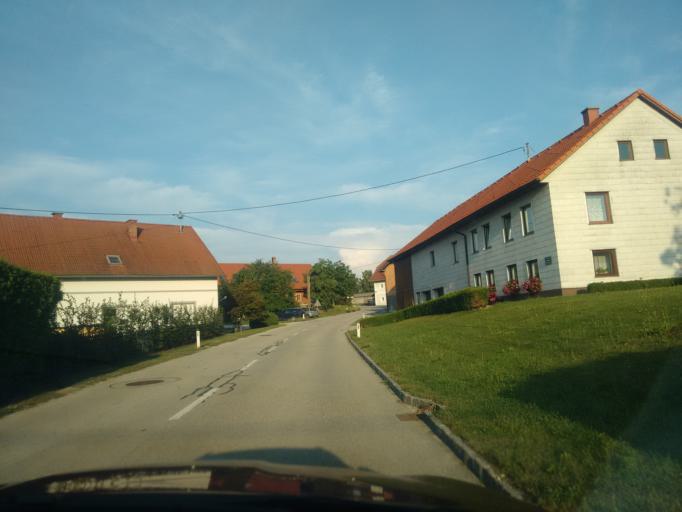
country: AT
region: Upper Austria
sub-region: Wels-Land
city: Offenhausen
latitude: 48.1579
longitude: 13.8012
